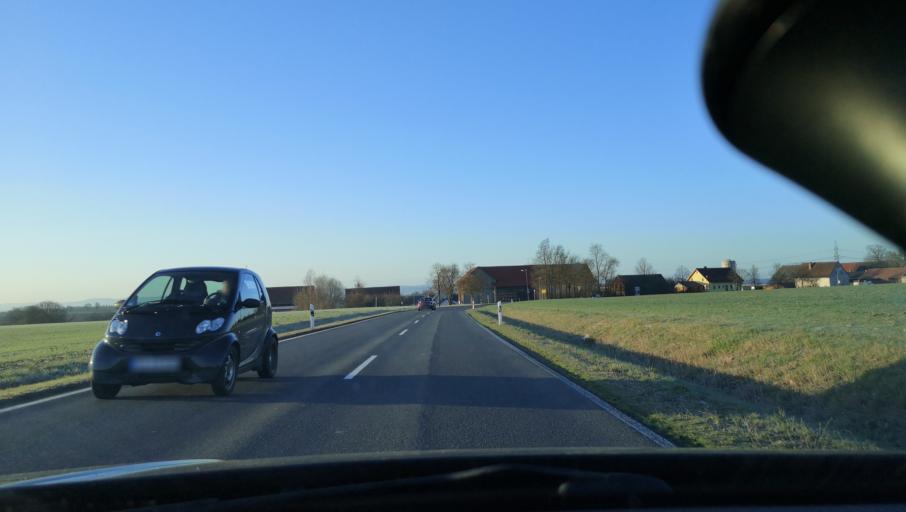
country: DE
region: Bavaria
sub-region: Upper Franconia
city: Rodental
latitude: 50.2571
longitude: 11.0852
